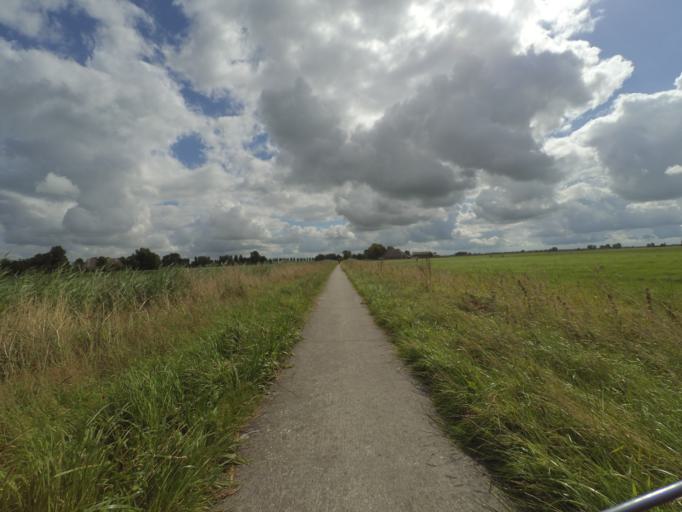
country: NL
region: Friesland
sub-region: Gemeente Kollumerland en Nieuwkruisland
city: Kollum
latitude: 53.2707
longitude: 6.1842
